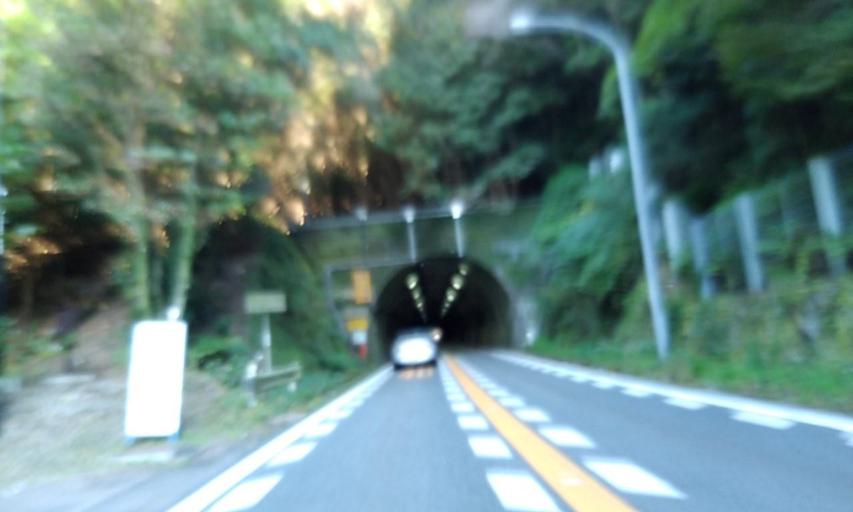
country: JP
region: Mie
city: Ise
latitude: 34.4104
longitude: 136.7647
